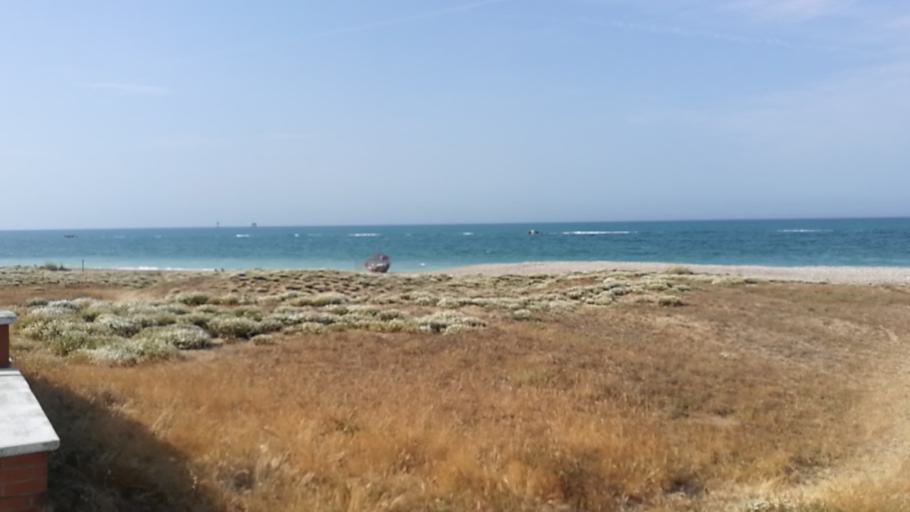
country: IT
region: Abruzzo
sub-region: Provincia di Chieti
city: Casalbordino-Miracoli
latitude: 42.2004
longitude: 14.6156
